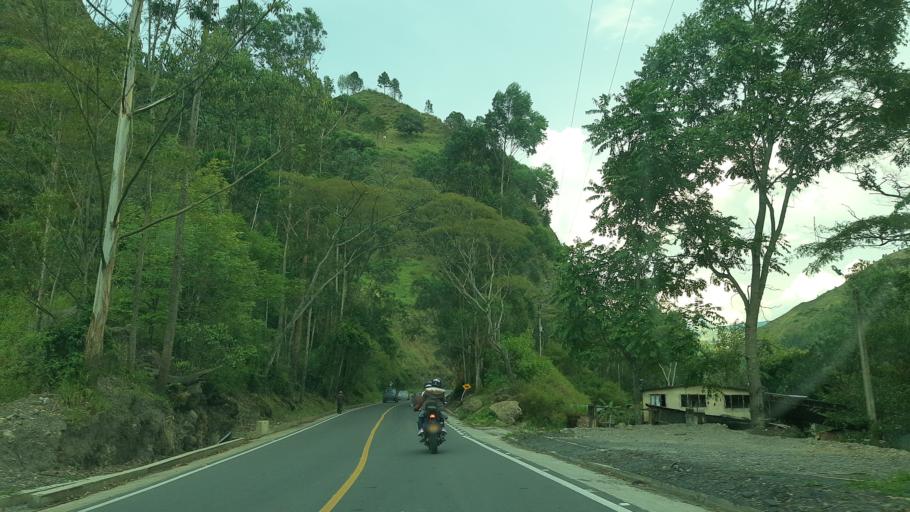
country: CO
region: Boyaca
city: Somondoco
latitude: 5.0095
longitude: -73.3987
